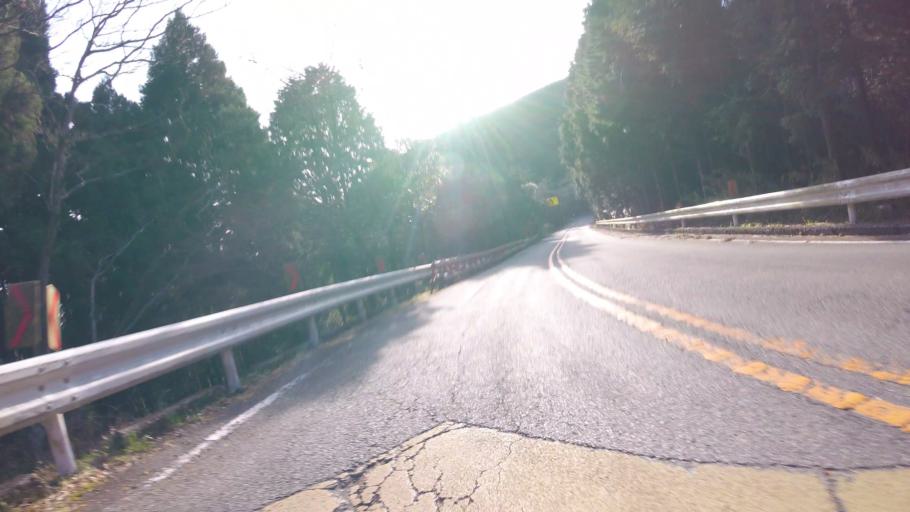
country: JP
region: Kanagawa
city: Yugawara
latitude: 35.1199
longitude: 139.0434
